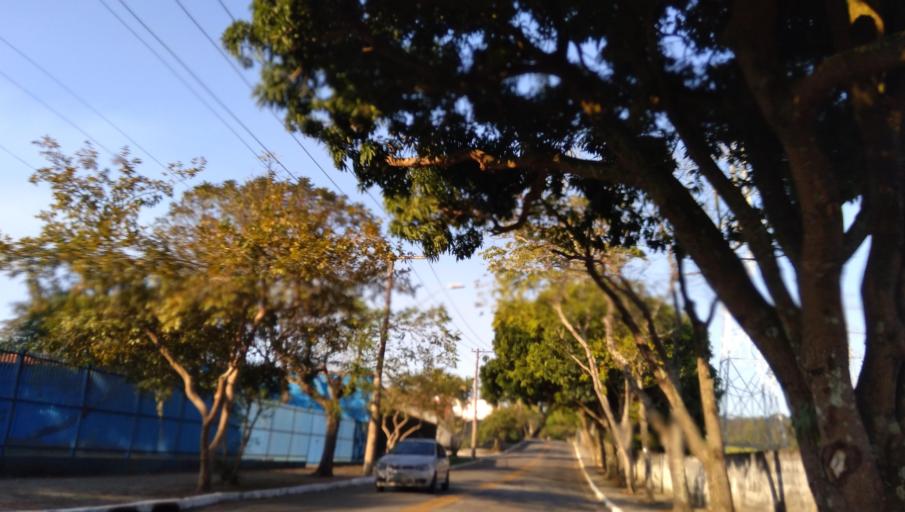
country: BR
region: Sao Paulo
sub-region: Sao Jose Dos Campos
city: Sao Jose dos Campos
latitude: -23.1839
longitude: -45.8311
